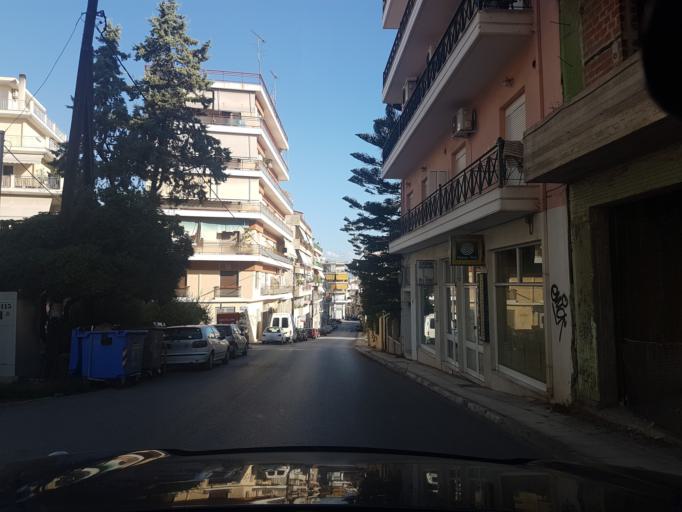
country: GR
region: Central Greece
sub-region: Nomos Evvoias
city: Chalkida
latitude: 38.4671
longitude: 23.6016
